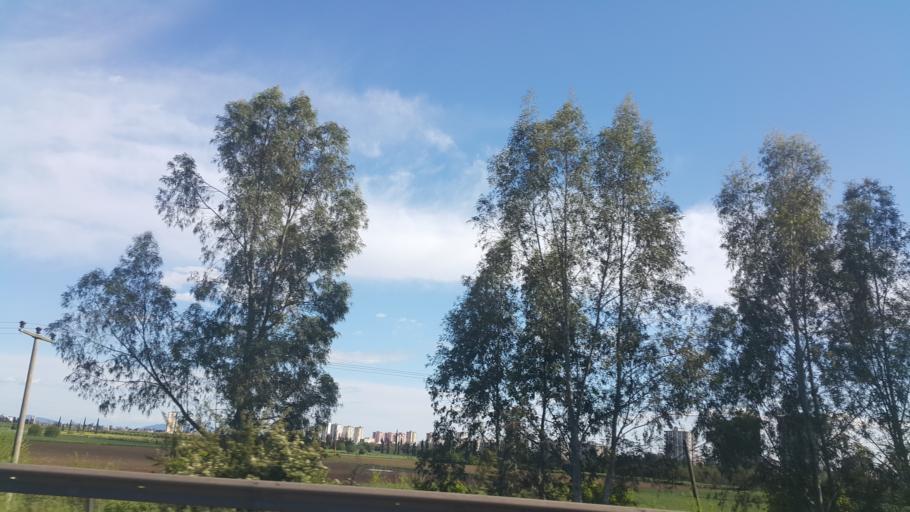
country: TR
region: Adana
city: Adana
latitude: 37.0269
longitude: 35.3719
